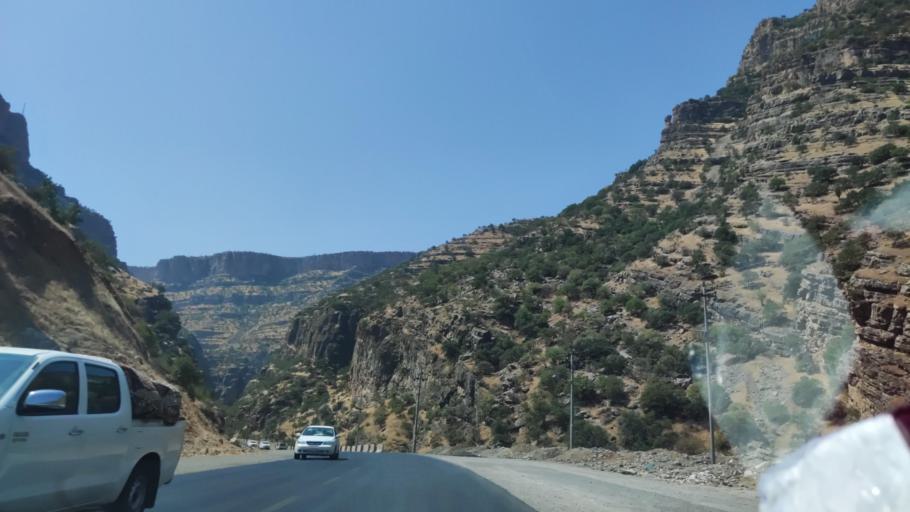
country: IQ
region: Arbil
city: Ruwandiz
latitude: 36.6414
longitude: 44.4928
